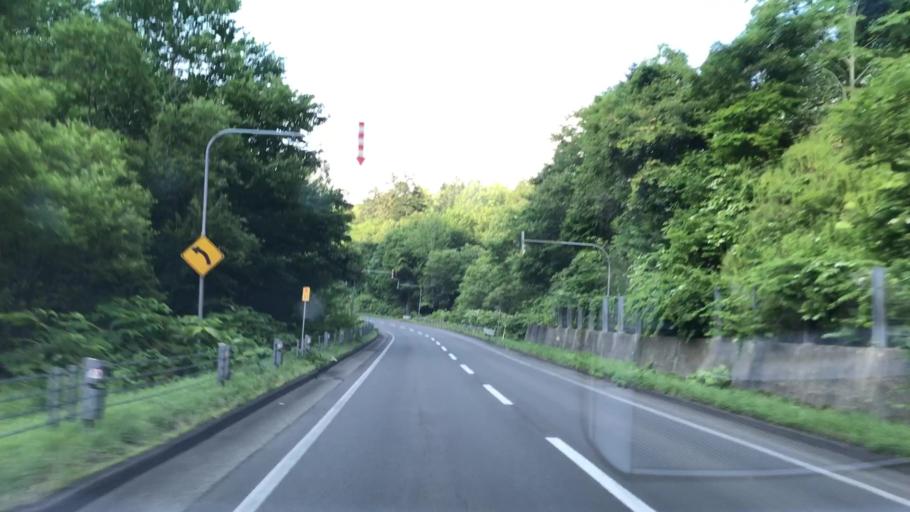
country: JP
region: Hokkaido
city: Iwamizawa
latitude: 42.8956
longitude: 142.1254
